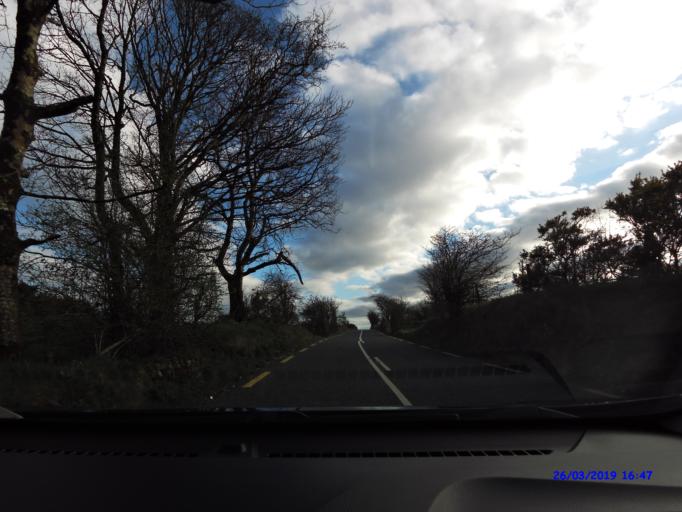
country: IE
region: Connaught
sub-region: Maigh Eo
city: Ballyhaunis
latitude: 53.8192
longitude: -8.7637
